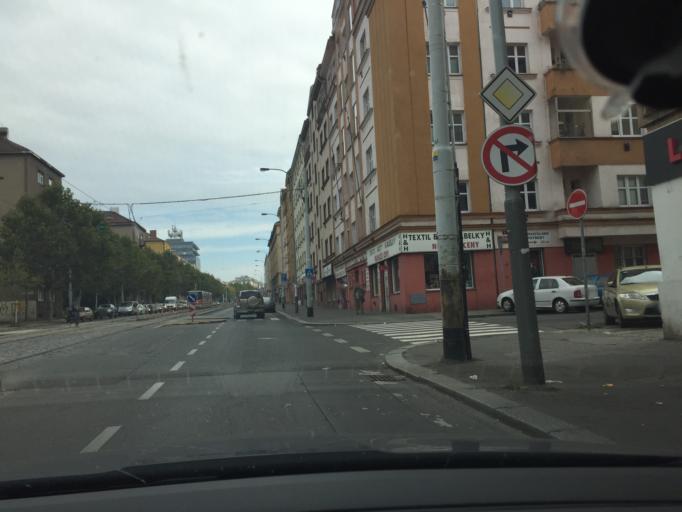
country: CZ
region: Praha
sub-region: Praha 8
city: Liben
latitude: 50.0907
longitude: 14.4703
